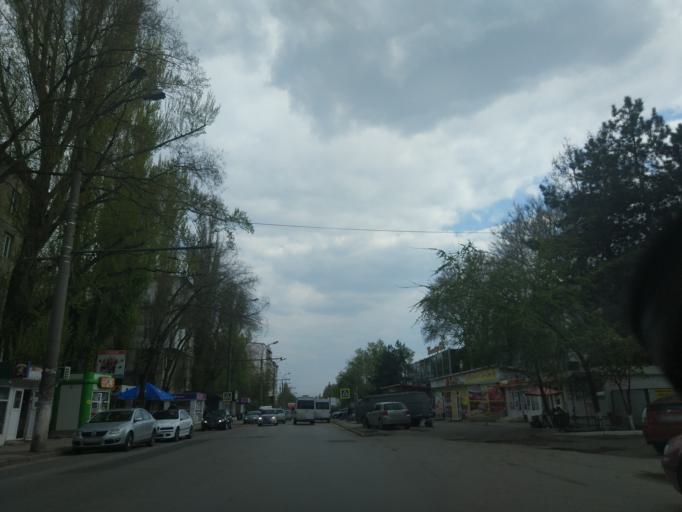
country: MD
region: Chisinau
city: Chisinau
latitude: 46.9844
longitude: 28.8764
